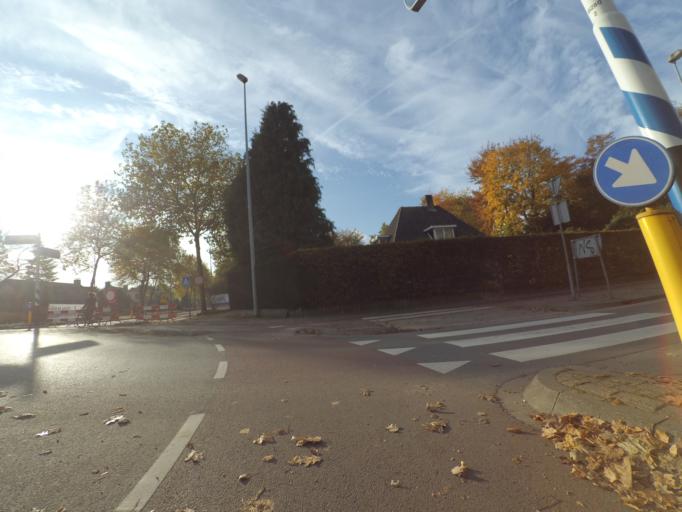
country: NL
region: Gelderland
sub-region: Gemeente Ede
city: Bennekom
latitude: 52.0078
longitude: 5.6741
